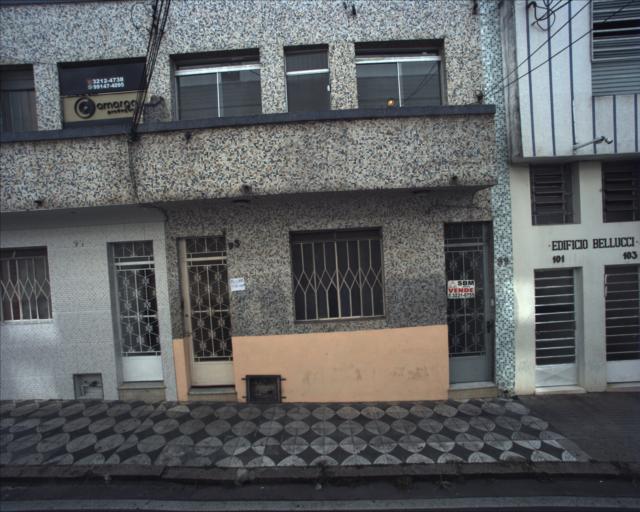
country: BR
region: Sao Paulo
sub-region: Sorocaba
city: Sorocaba
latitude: -23.4971
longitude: -47.4573
